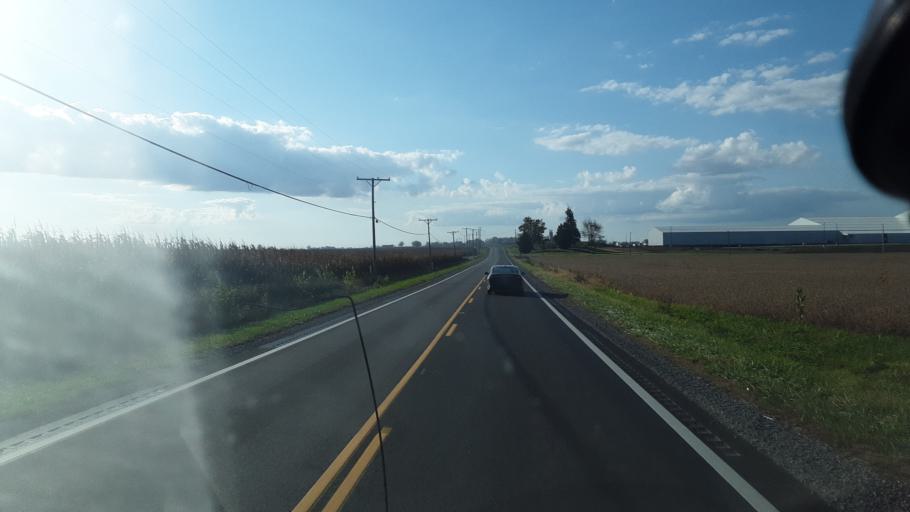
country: US
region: Ohio
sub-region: Fayette County
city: Jeffersonville
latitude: 39.6314
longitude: -83.5312
